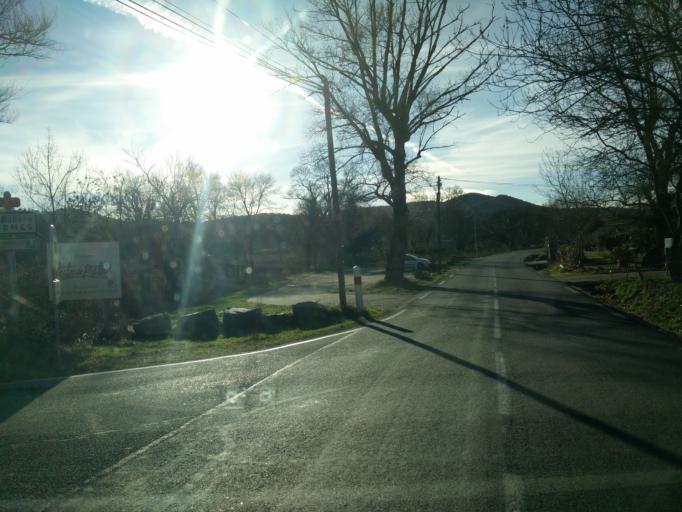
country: FR
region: Provence-Alpes-Cote d'Azur
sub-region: Departement du Var
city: Collobrieres
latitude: 43.2360
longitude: 6.2867
